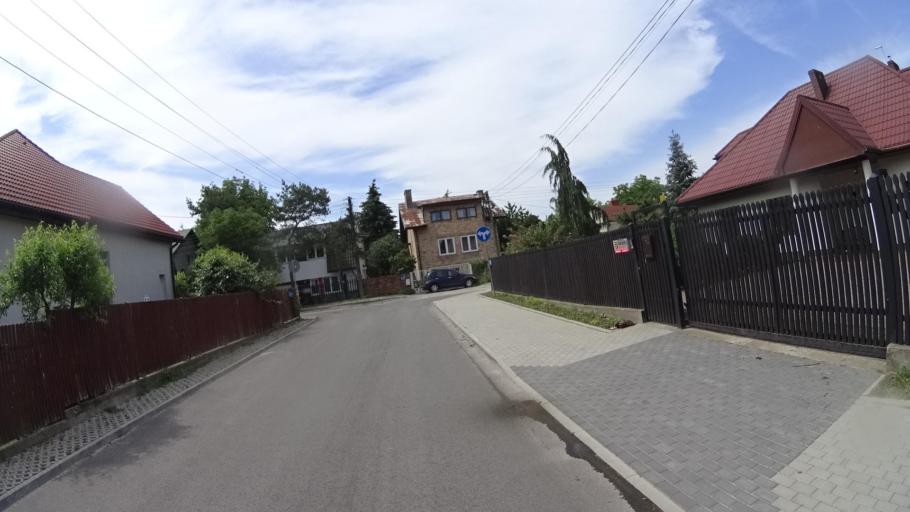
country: PL
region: Masovian Voivodeship
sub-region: Powiat pruszkowski
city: Raszyn
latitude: 52.1715
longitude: 20.9263
